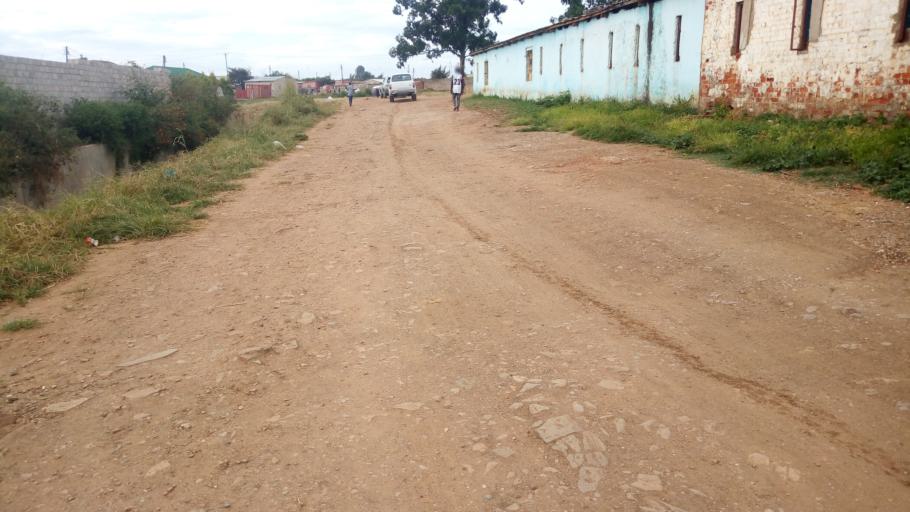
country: ZM
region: Lusaka
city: Lusaka
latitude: -15.3944
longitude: 28.2863
